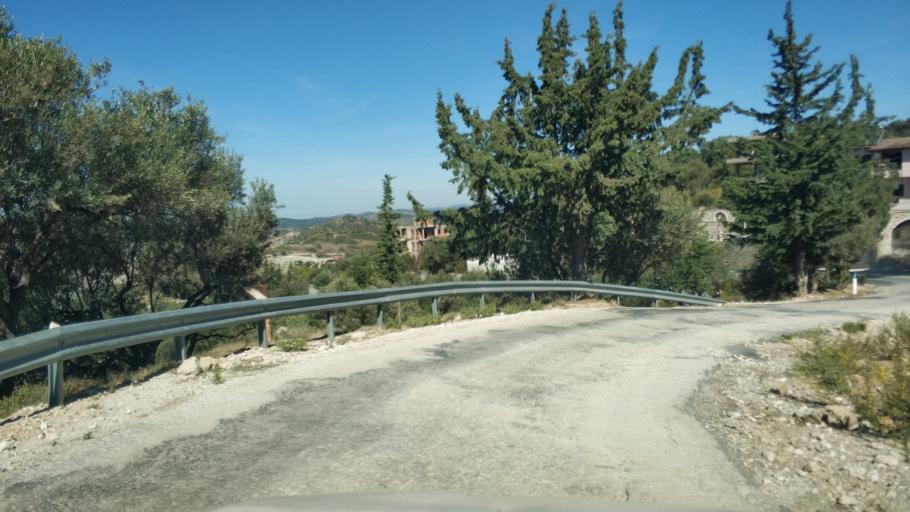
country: AL
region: Vlore
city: Vlore
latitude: 40.4498
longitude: 19.5158
